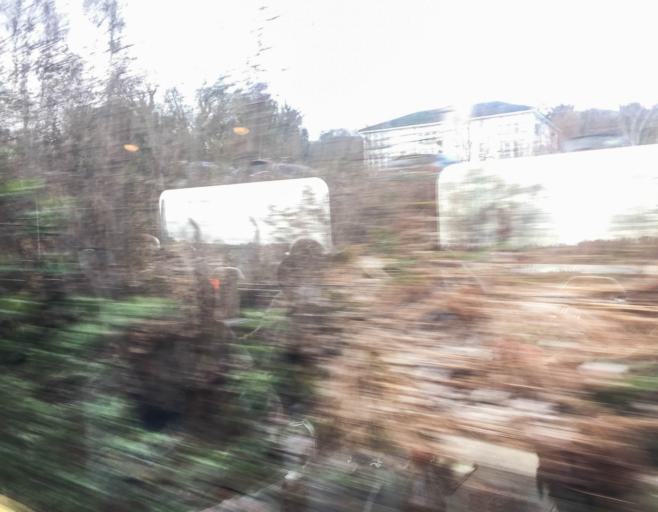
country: GB
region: Scotland
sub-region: Renfrewshire
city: Bishopton
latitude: 55.9309
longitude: -4.4994
